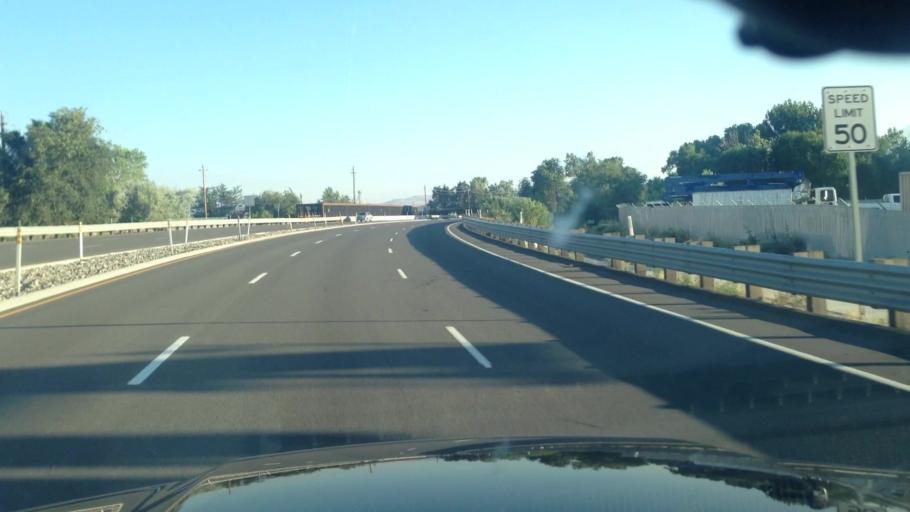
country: US
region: Nevada
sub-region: Washoe County
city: Sparks
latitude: 39.5191
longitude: -119.7404
